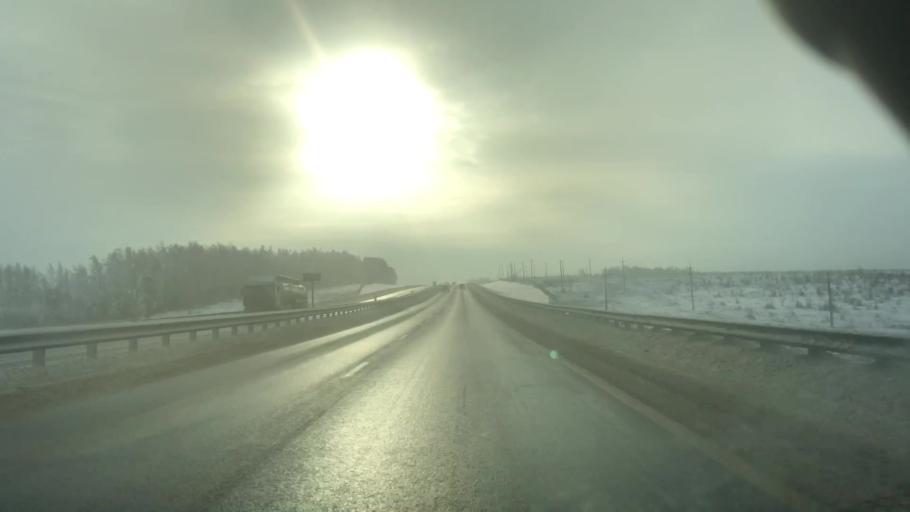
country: RU
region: Tula
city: Venev
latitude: 54.3192
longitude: 38.1544
